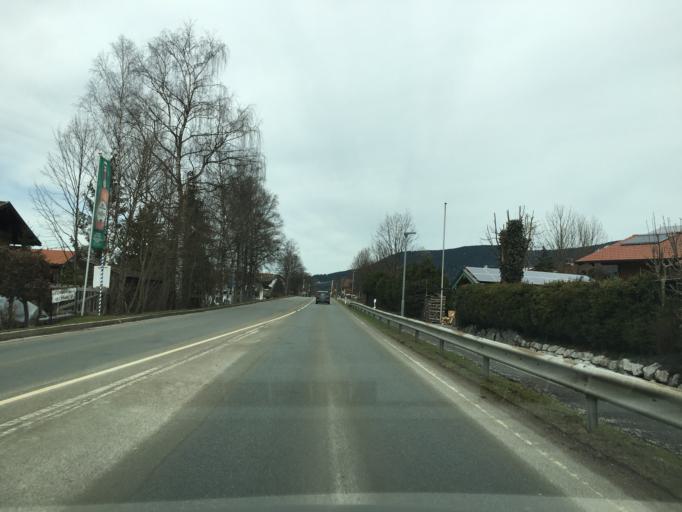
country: DE
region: Bavaria
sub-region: Upper Bavaria
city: Inzell
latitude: 47.7601
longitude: 12.7498
